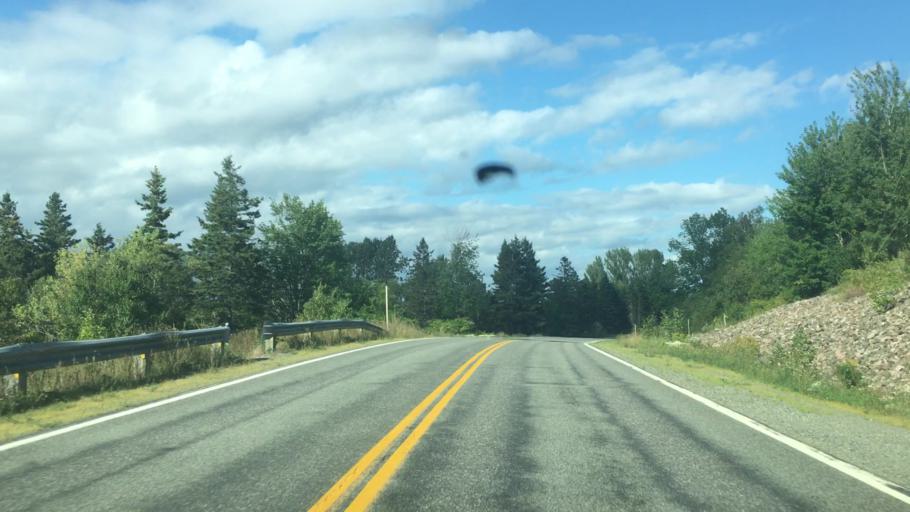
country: CA
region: Nova Scotia
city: Sydney
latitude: 45.8729
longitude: -60.6056
